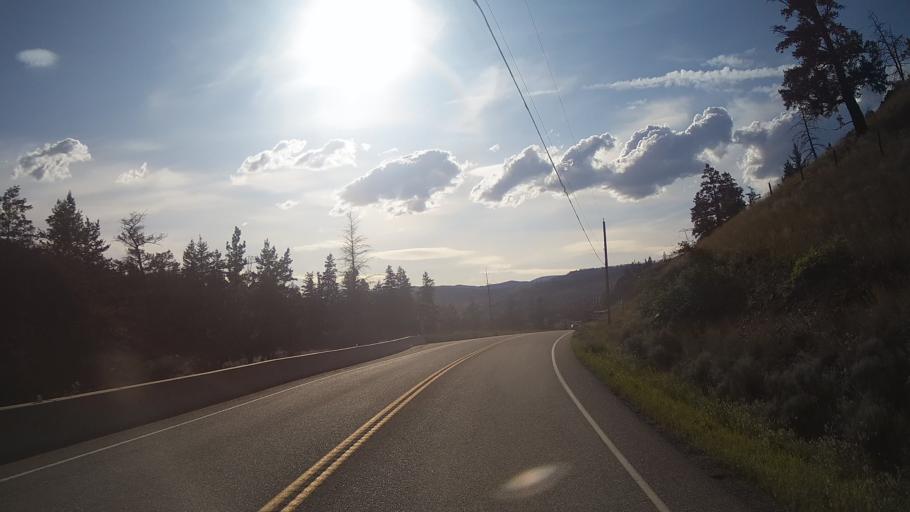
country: CA
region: British Columbia
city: Cache Creek
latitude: 50.8842
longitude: -121.4270
